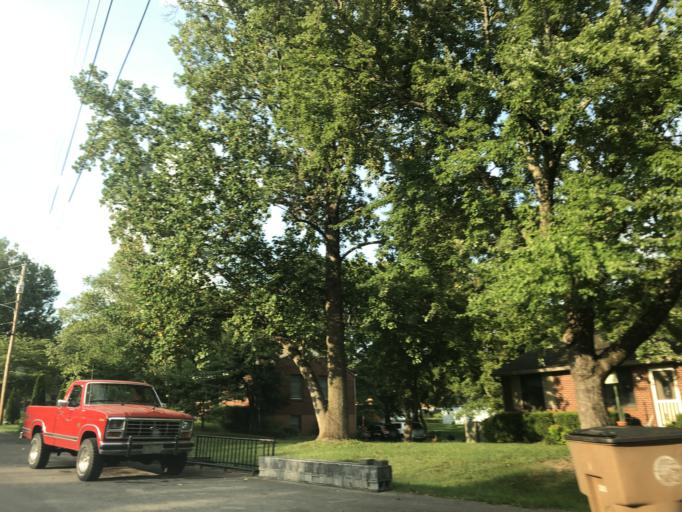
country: US
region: Tennessee
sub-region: Davidson County
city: Lakewood
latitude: 36.1536
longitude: -86.6722
